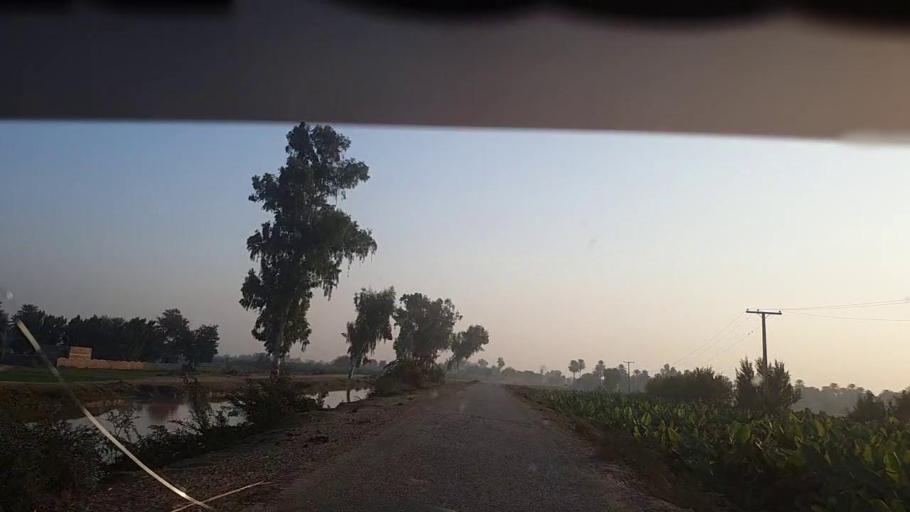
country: PK
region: Sindh
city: Ranipur
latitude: 27.2366
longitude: 68.5492
